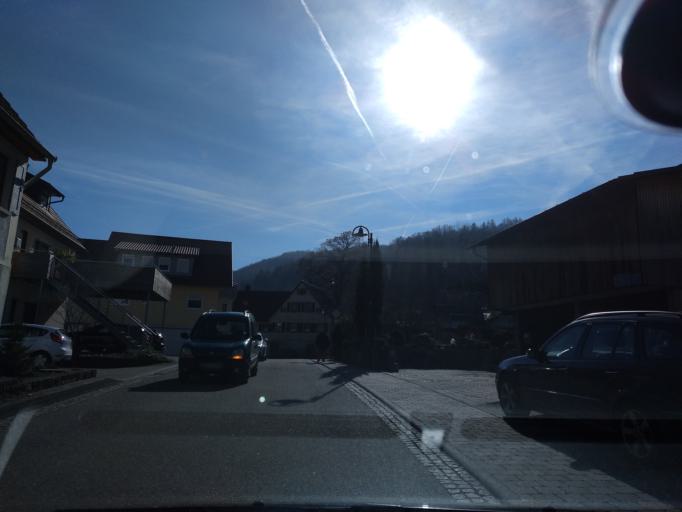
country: DE
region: Baden-Wuerttemberg
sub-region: Regierungsbezirk Stuttgart
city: Mainhardt
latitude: 49.1191
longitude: 9.5208
